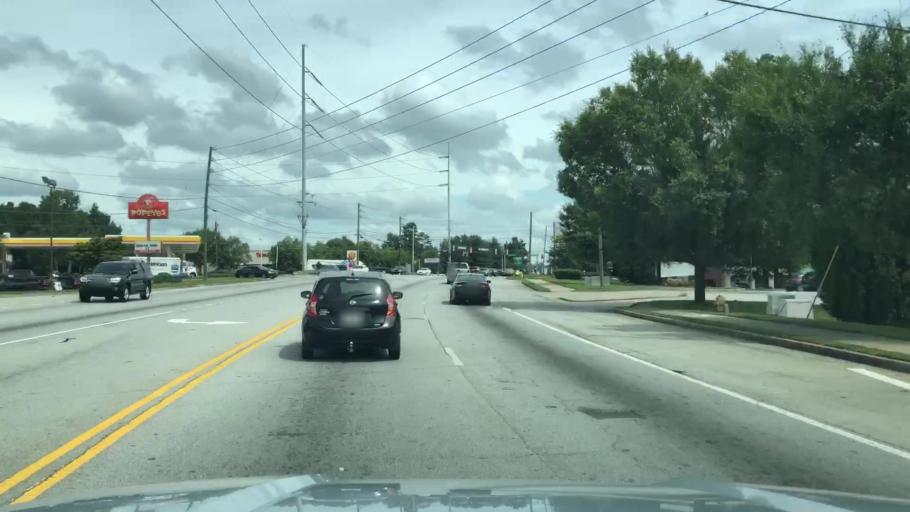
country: US
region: Georgia
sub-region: DeKalb County
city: Redan
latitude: 33.6994
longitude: -84.1727
